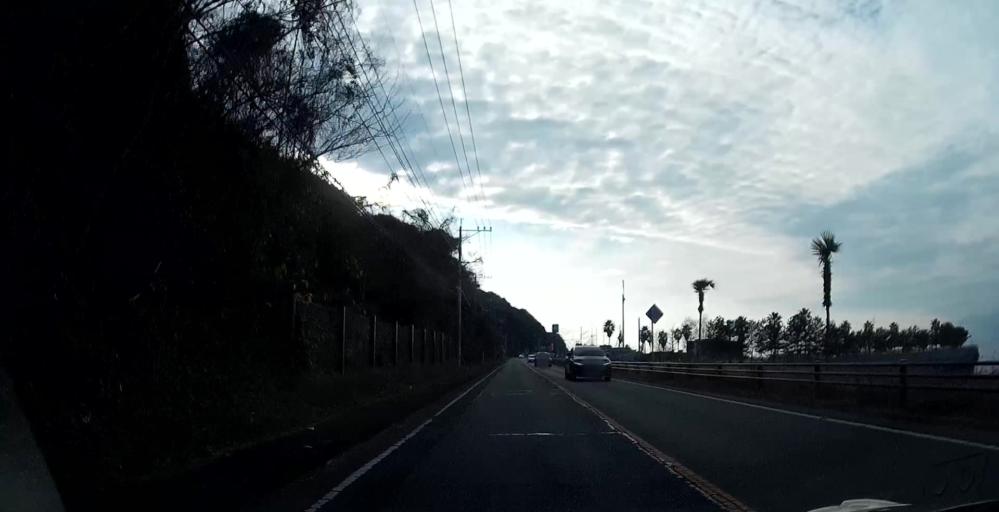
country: JP
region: Kumamoto
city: Matsubase
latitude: 32.6629
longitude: 130.5262
